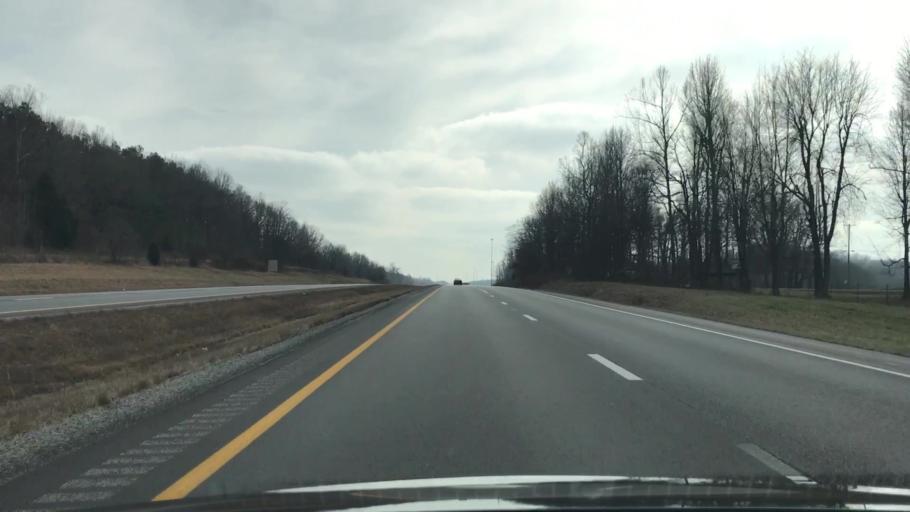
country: US
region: Kentucky
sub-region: Hopkins County
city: Nortonville
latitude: 37.2311
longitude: -87.4456
